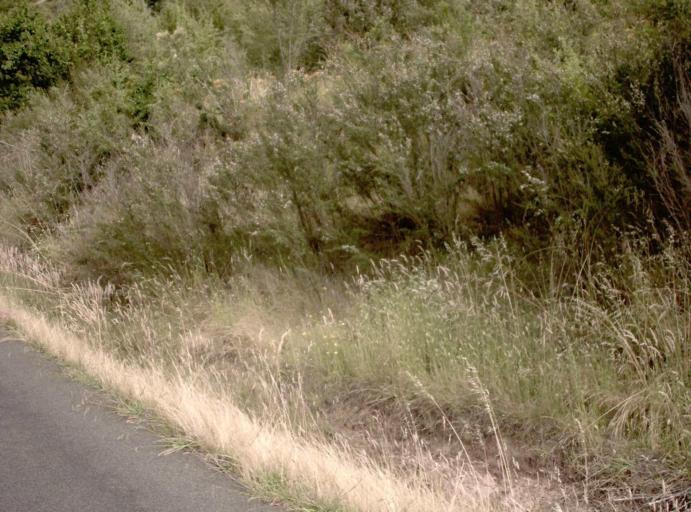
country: AU
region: Victoria
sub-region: Wellington
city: Heyfield
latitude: -37.6253
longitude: 146.6220
